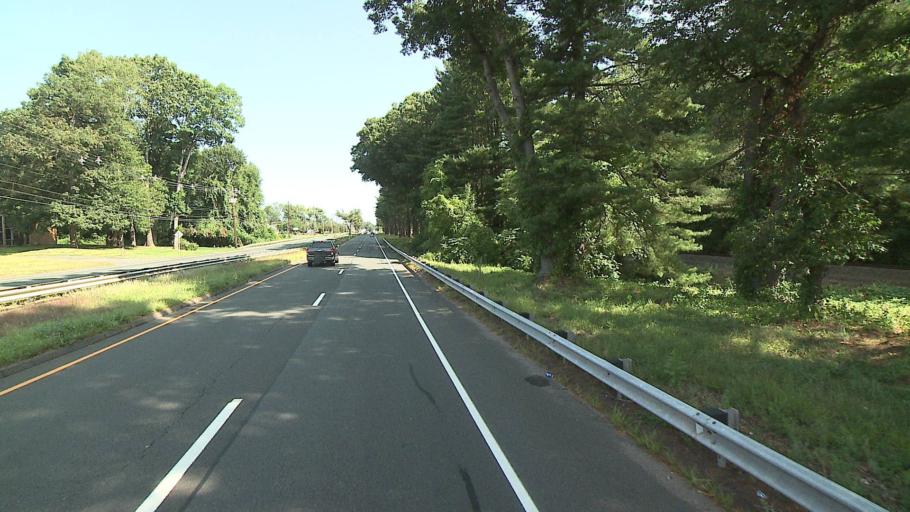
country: US
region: Connecticut
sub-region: Hartford County
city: South Windsor
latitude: 41.8377
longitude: -72.6024
